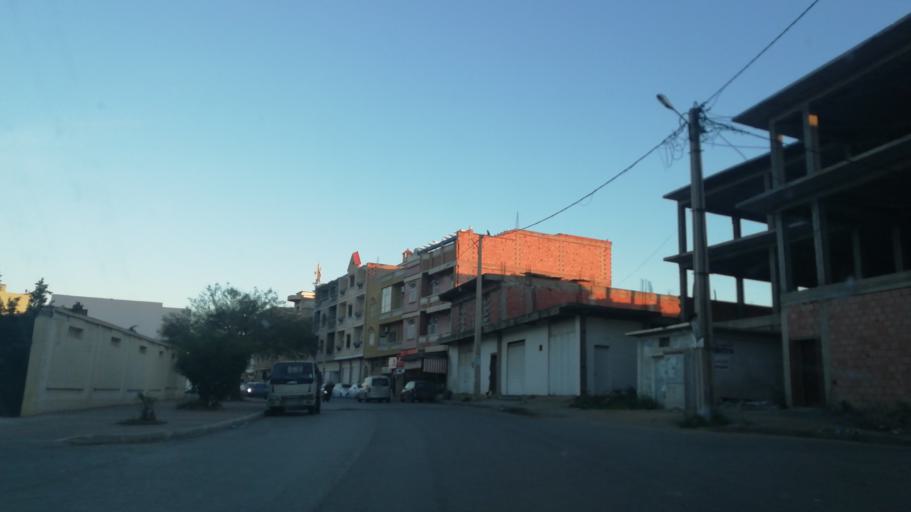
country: DZ
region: Oran
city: Oran
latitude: 35.6985
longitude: -0.5969
